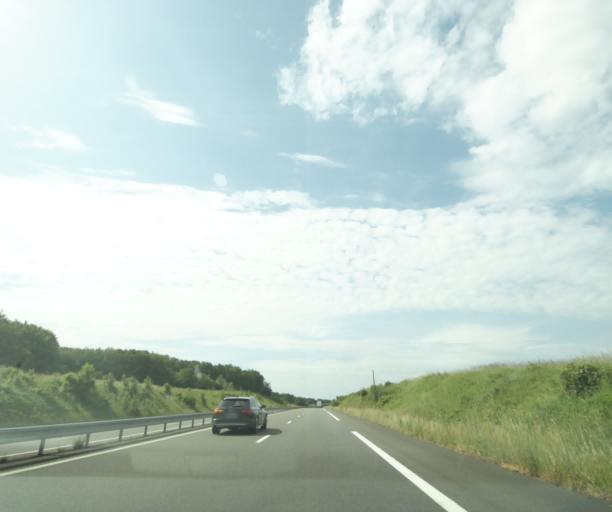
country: FR
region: Pays de la Loire
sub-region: Departement de Maine-et-Loire
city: Baune
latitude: 47.5026
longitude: -0.2847
